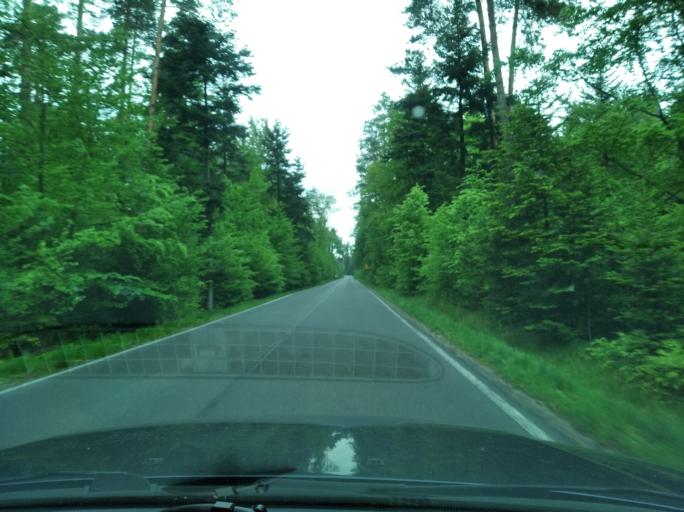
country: PL
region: Subcarpathian Voivodeship
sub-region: Powiat kolbuszowski
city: Kolbuszowa
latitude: 50.1648
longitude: 21.7595
